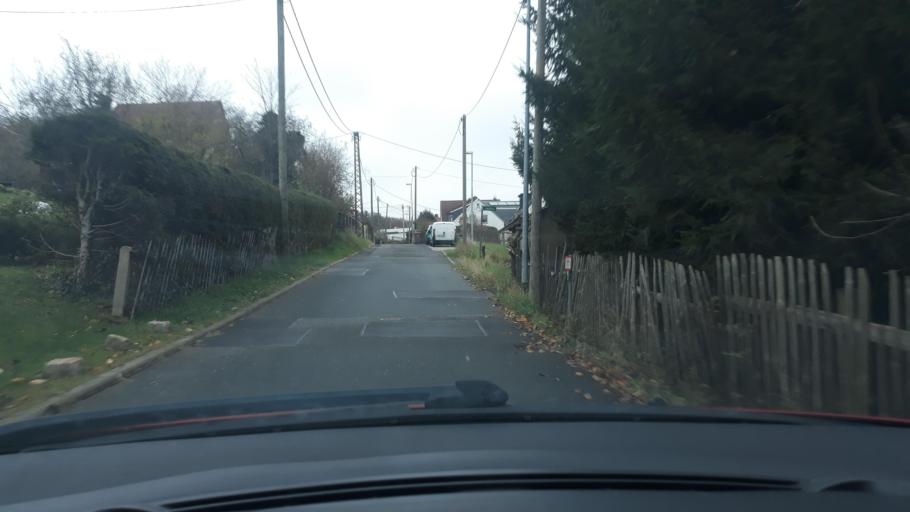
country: DE
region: Saxony
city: Wilkau-Hasslau
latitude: 50.6684
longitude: 12.5495
